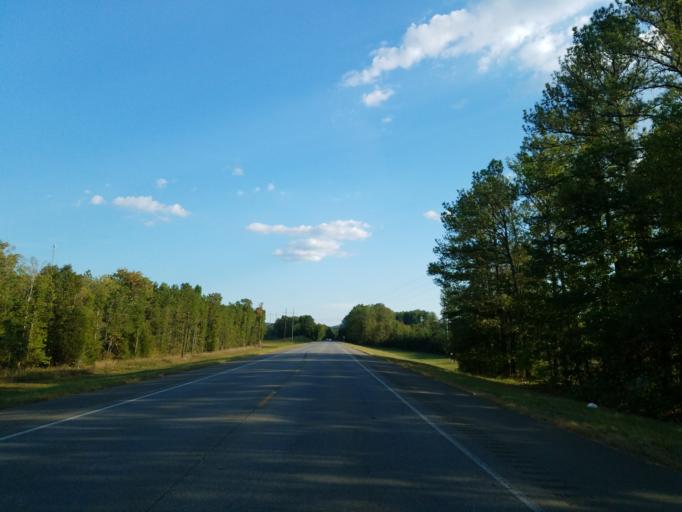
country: US
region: Georgia
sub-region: Murray County
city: Chatsworth
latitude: 34.6468
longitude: -84.7168
